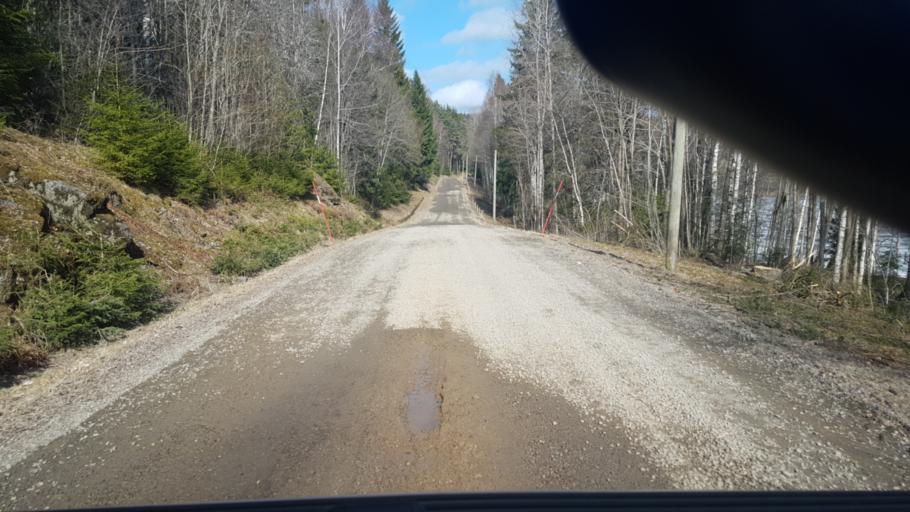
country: SE
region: Vaermland
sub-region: Eda Kommun
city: Amotfors
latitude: 59.8107
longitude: 12.4460
